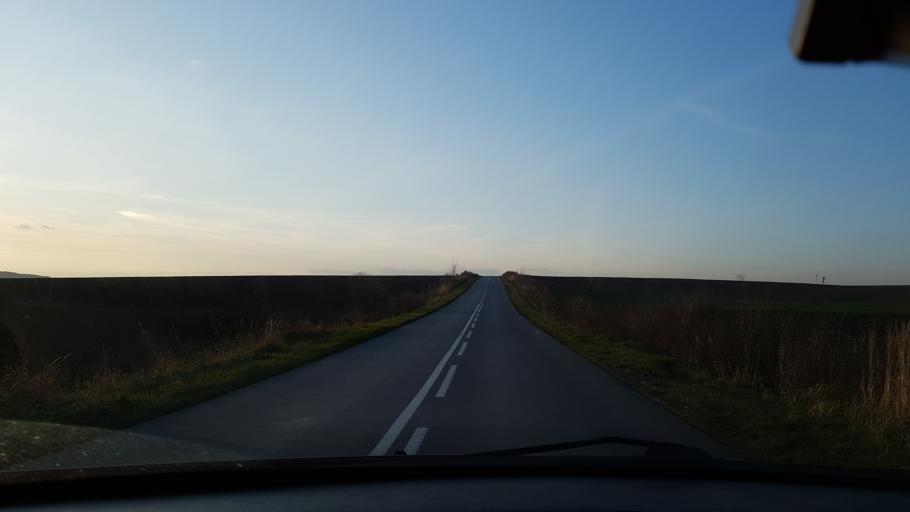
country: PL
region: Lower Silesian Voivodeship
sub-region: Powiat zabkowicki
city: Henrykow
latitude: 50.6694
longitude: 16.9727
